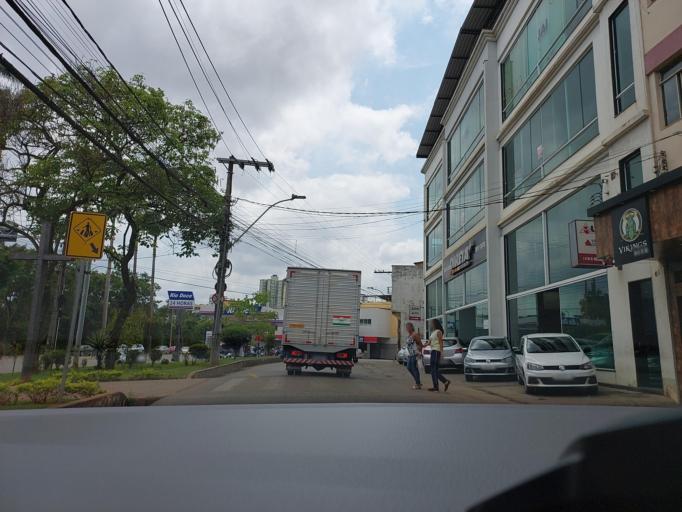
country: BR
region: Minas Gerais
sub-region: Ponte Nova
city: Ponte Nova
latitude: -20.4153
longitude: -42.9019
